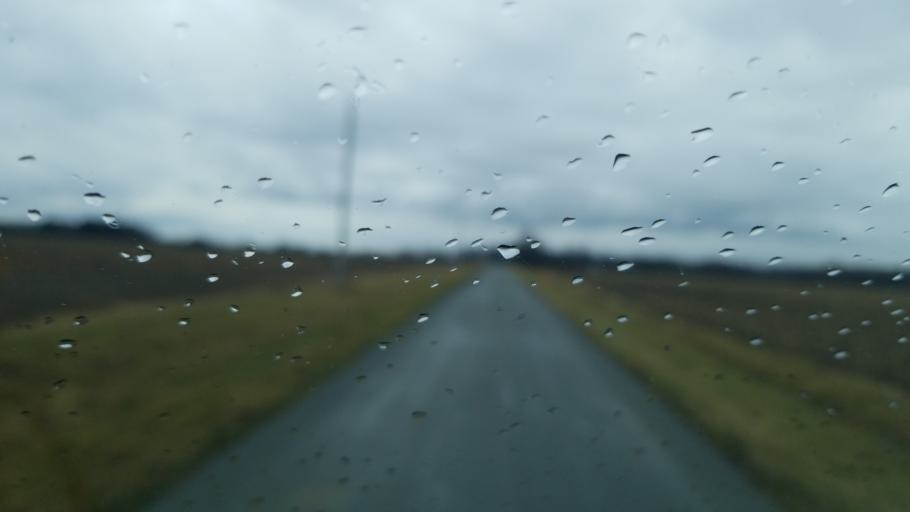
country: US
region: Ohio
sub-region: Hardin County
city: Forest
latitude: 40.7509
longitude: -83.4002
